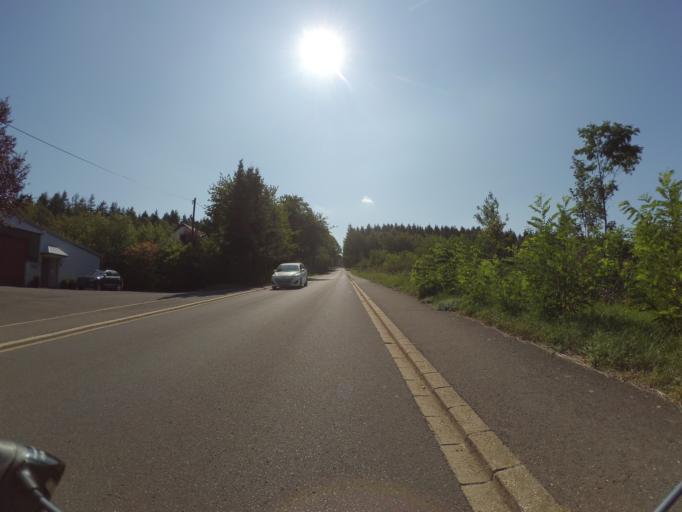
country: DE
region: Rheinland-Pfalz
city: Morbach
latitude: 49.7738
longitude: 7.1033
